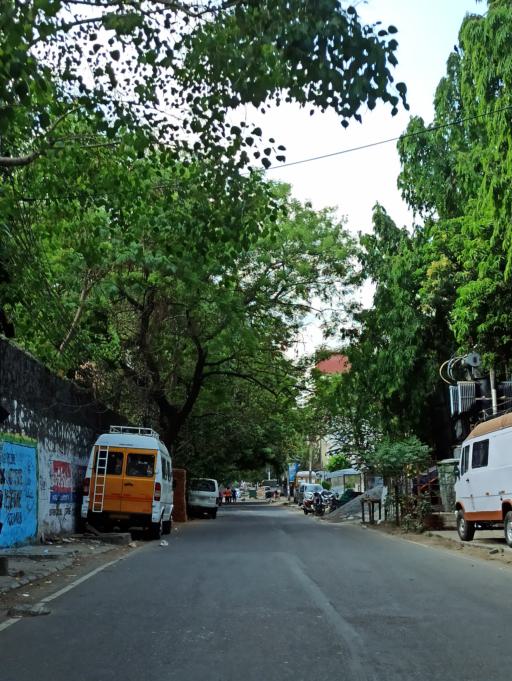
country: IN
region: Tamil Nadu
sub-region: Chennai
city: Chetput
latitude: 13.0505
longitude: 80.2075
